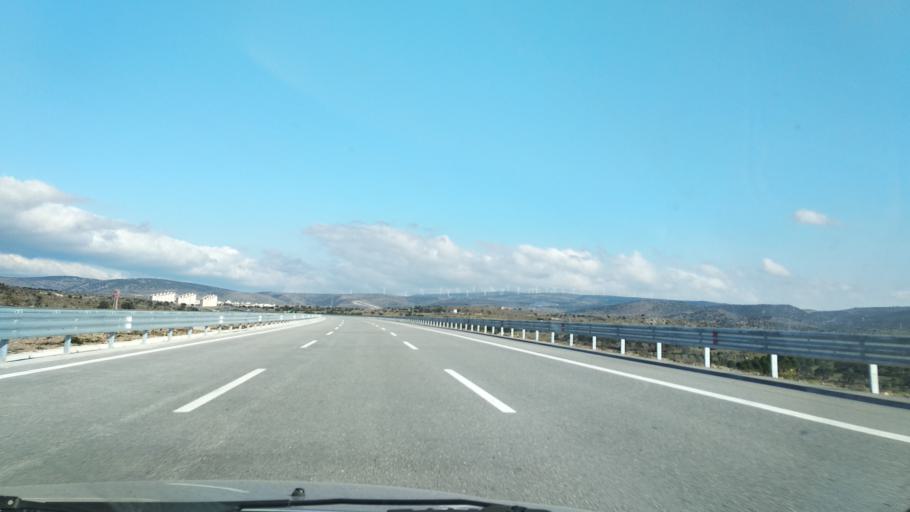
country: TR
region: Izmir
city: Yenisakran
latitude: 38.8629
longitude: 27.0772
